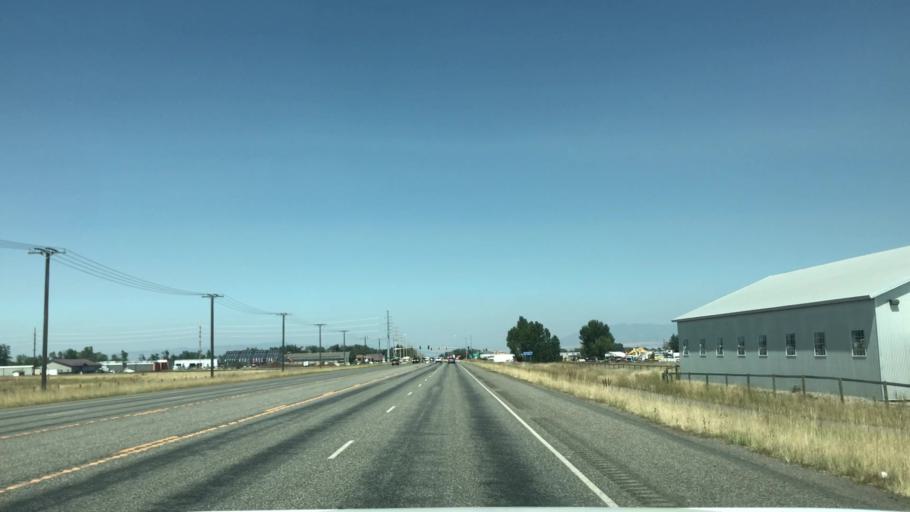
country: US
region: Montana
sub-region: Gallatin County
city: Four Corners
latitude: 45.6965
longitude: -111.1854
